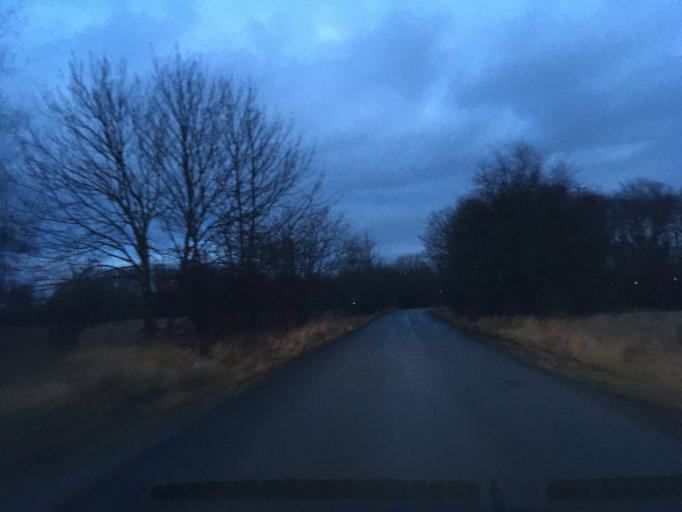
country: EE
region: Harju
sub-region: Tallinna linn
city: Tallinn
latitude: 59.4406
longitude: 24.8118
